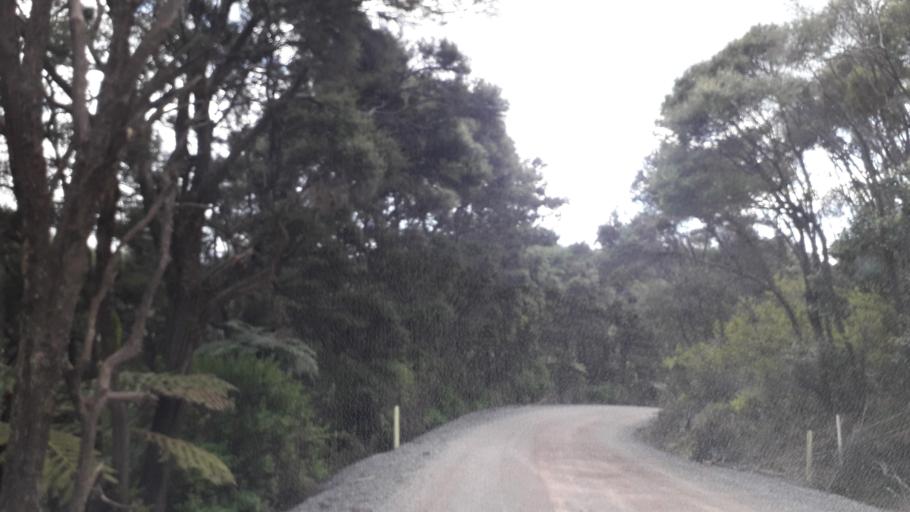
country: NZ
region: Northland
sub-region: Far North District
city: Paihia
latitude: -35.3154
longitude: 174.2248
